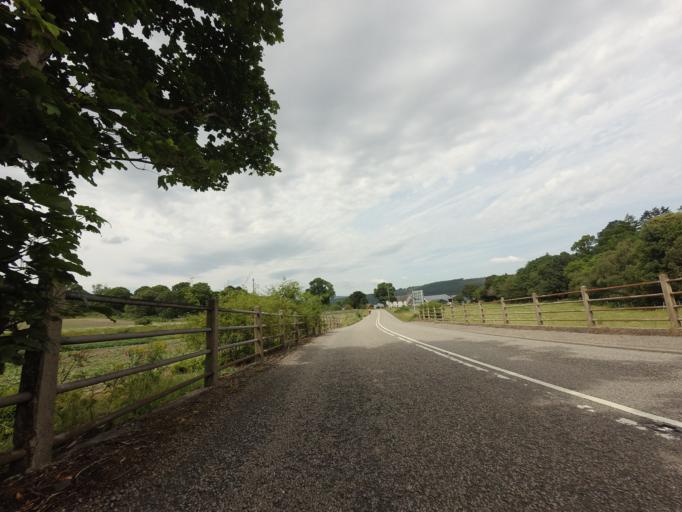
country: GB
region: Scotland
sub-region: Highland
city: Alness
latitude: 57.8573
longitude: -4.3120
